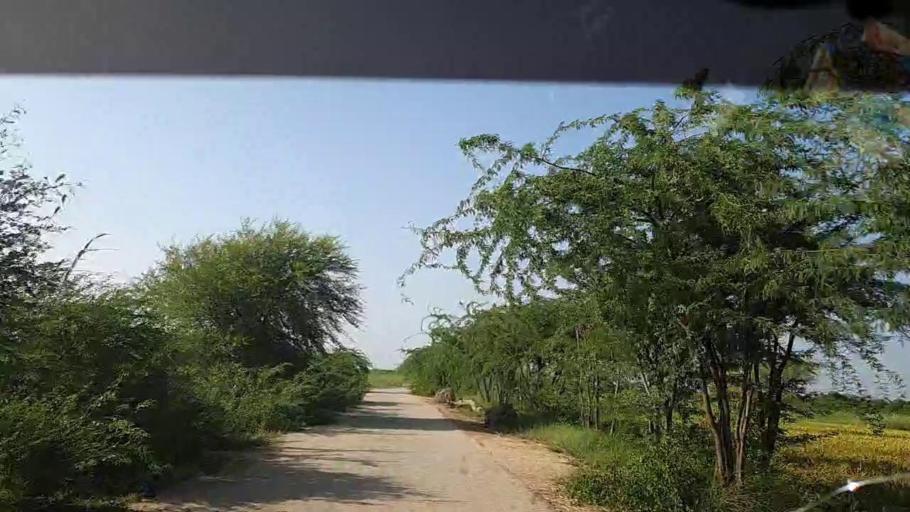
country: PK
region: Sindh
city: Badin
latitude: 24.6862
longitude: 68.8421
